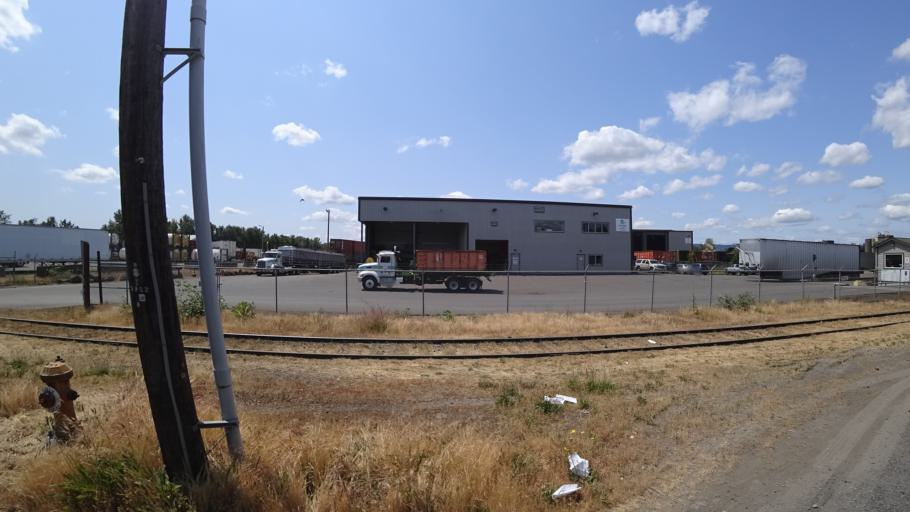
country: US
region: Washington
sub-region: Clark County
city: Vancouver
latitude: 45.6137
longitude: -122.7087
